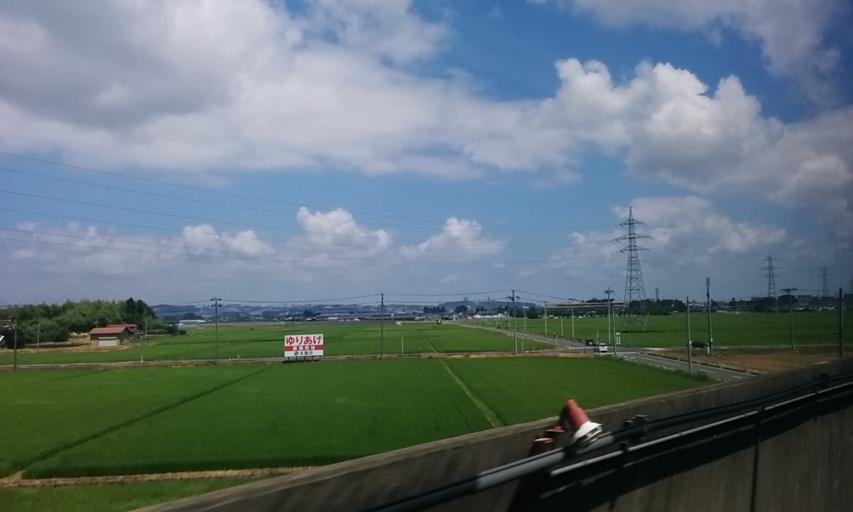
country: JP
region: Miyagi
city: Iwanuma
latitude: 38.1719
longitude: 140.8629
